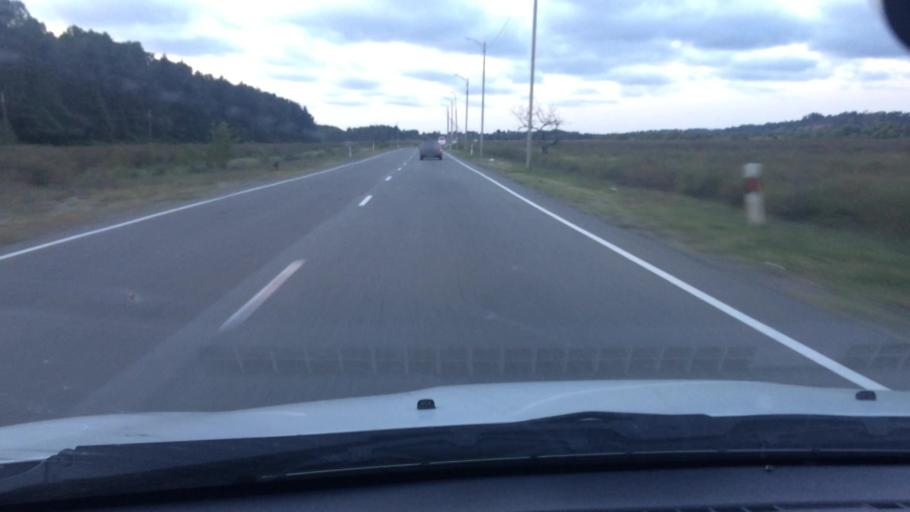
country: GE
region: Guria
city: Urek'i
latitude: 41.9462
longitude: 41.7706
